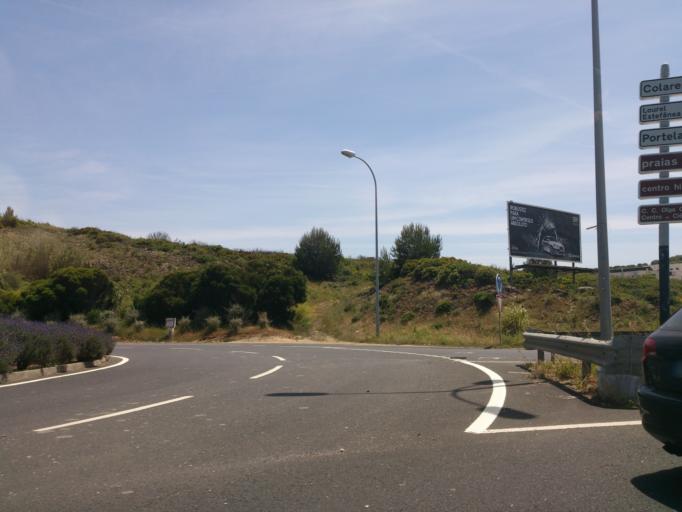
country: PT
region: Lisbon
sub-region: Sintra
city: Sintra
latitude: 38.8036
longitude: -9.3722
